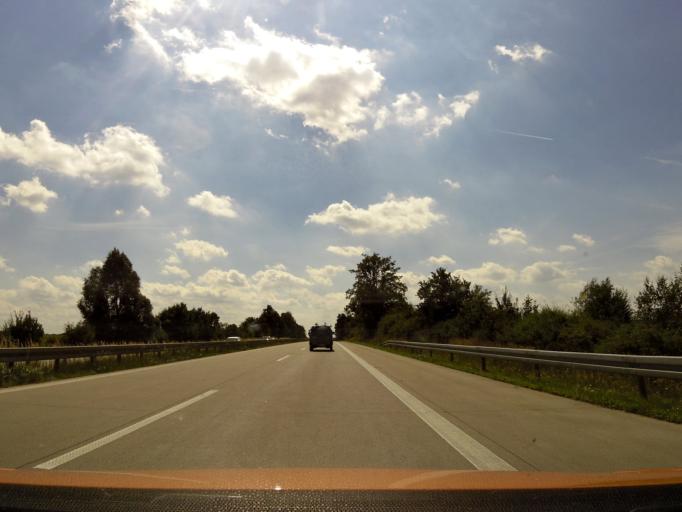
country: DE
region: Brandenburg
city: Althuttendorf
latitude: 53.0834
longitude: 13.8474
